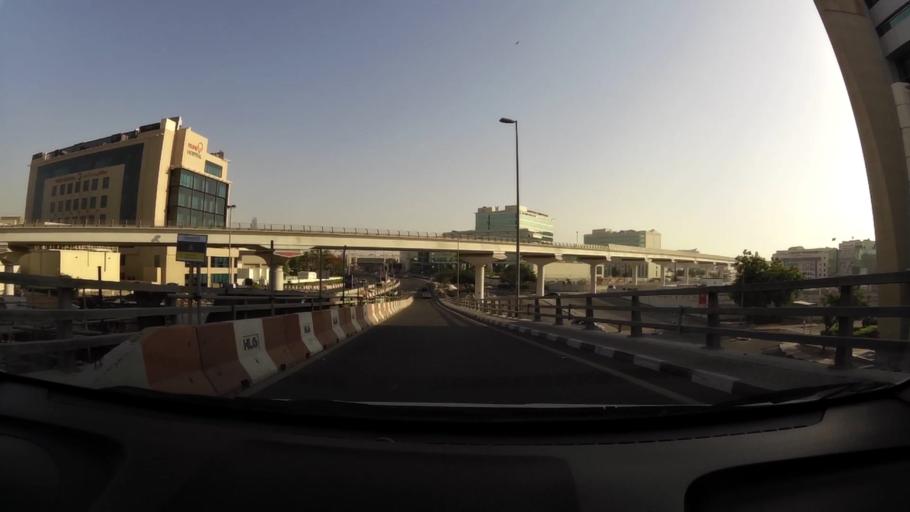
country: AE
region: Ash Shariqah
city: Sharjah
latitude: 25.2508
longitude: 55.3452
